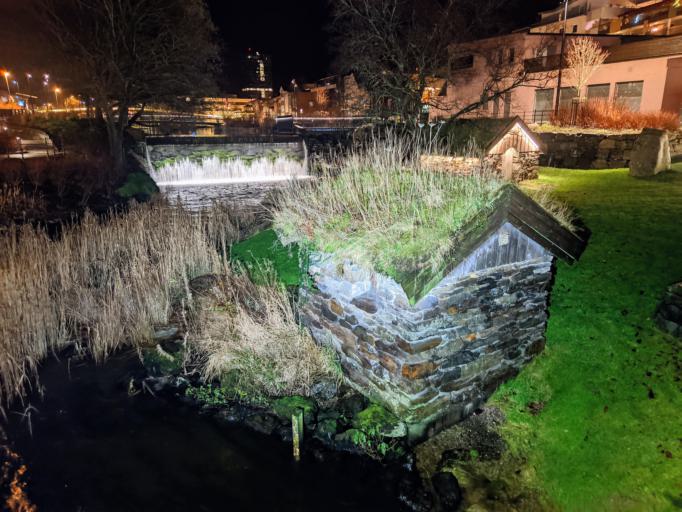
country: NO
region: Rogaland
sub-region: Time
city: Bryne
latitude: 58.7368
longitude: 5.6429
